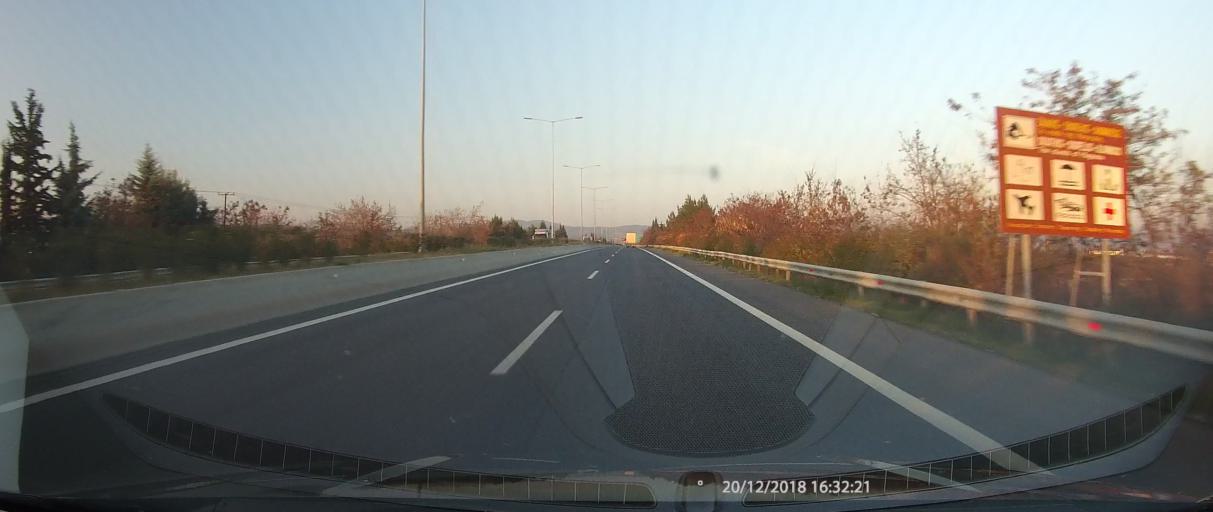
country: GR
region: Thessaly
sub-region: Nomos Magnisias
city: Evxinoupolis
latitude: 39.2430
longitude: 22.7340
